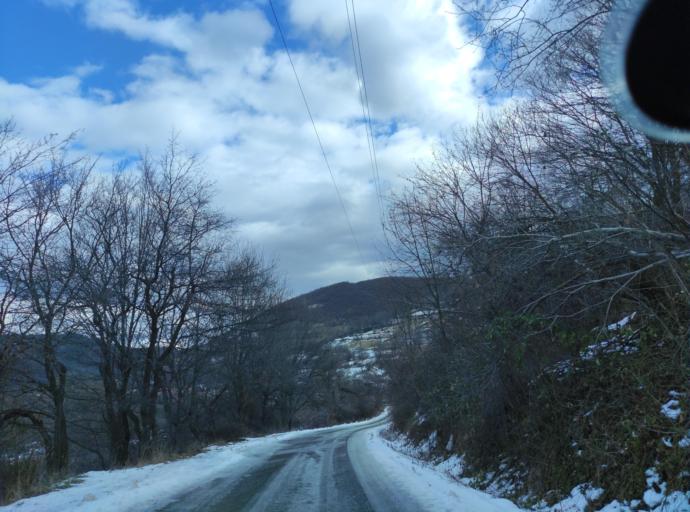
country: BG
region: Montana
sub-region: Obshtina Chiprovtsi
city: Chiprovtsi
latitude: 43.3774
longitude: 22.8713
